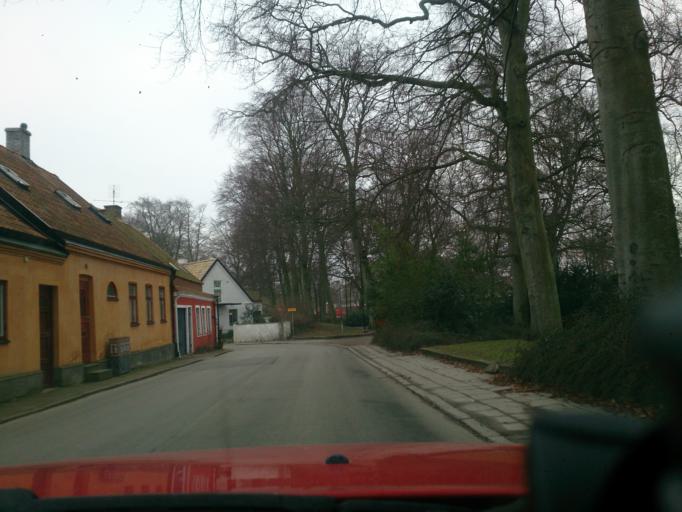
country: SE
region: Skane
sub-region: Ystads Kommun
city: Ystad
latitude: 55.4314
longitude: 13.8161
